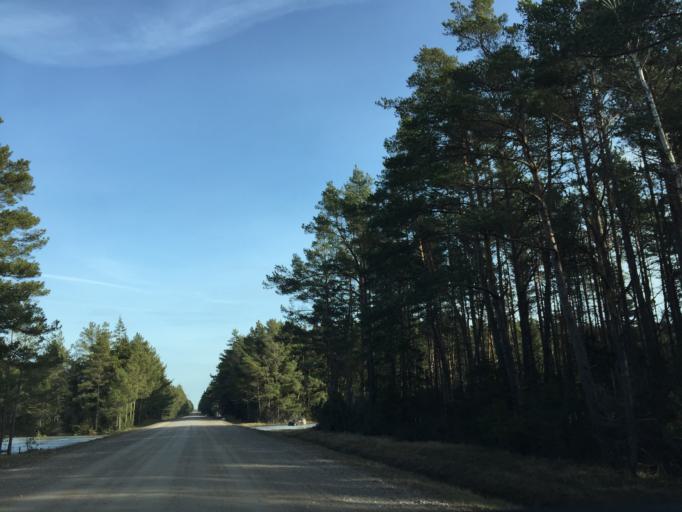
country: EE
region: Saare
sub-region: Kuressaare linn
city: Kuressaare
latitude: 58.3083
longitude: 21.9733
